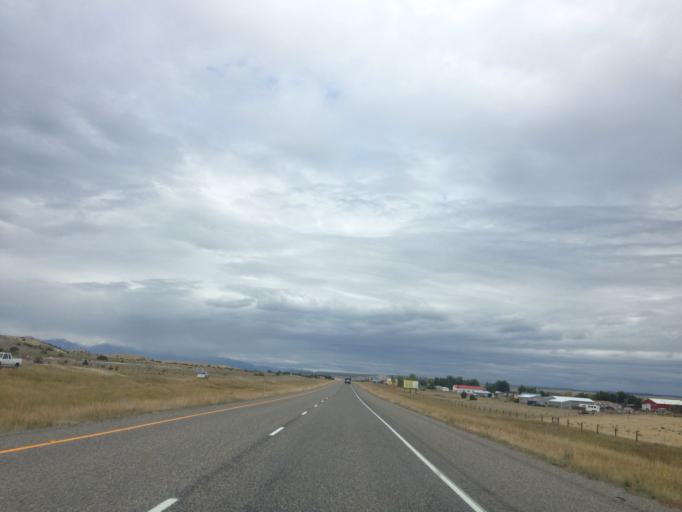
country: US
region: Montana
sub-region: Sweet Grass County
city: Big Timber
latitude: 45.7571
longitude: -109.7827
